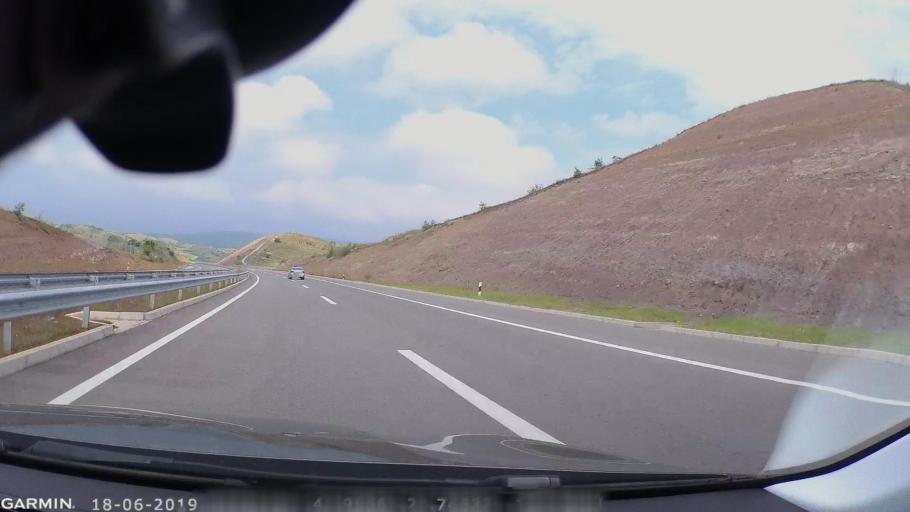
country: MK
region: Sveti Nikole
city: Gorobinci
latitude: 41.9265
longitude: 21.8341
